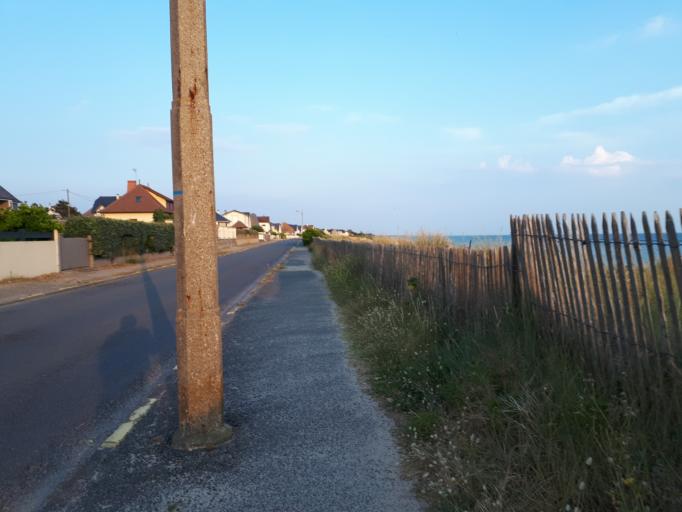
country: FR
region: Lower Normandy
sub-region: Departement de la Manche
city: Barneville-Plage
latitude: 49.3651
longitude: -1.7672
